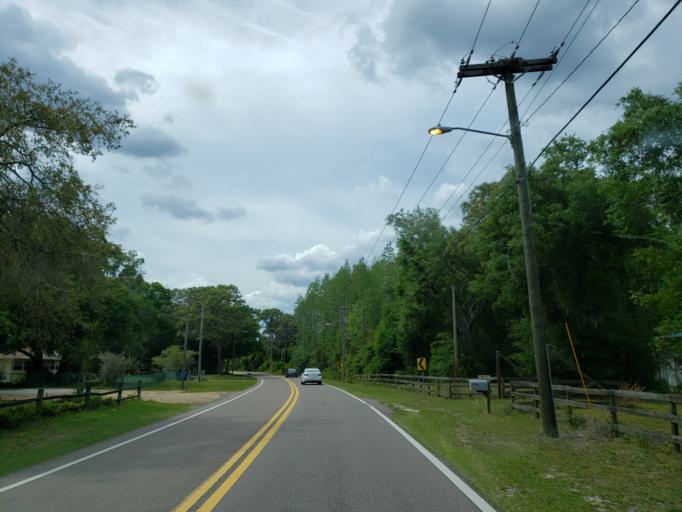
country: US
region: Florida
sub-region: Hillsborough County
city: Keystone
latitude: 28.1299
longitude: -82.6167
